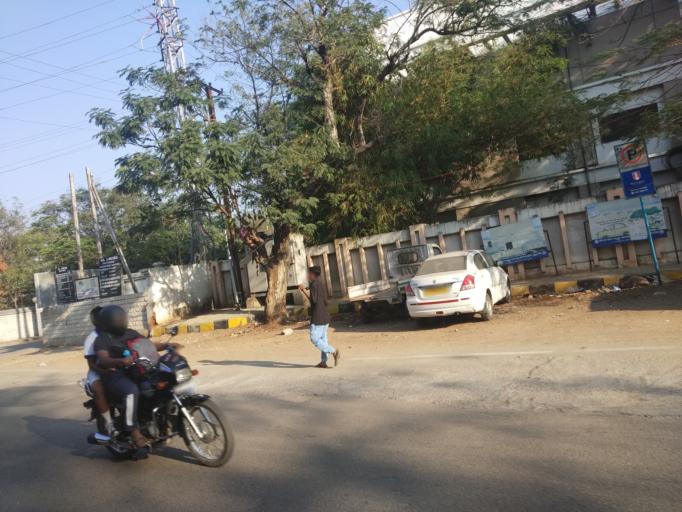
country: IN
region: Telangana
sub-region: Rangareddi
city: Kukatpalli
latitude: 17.4567
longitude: 78.4416
